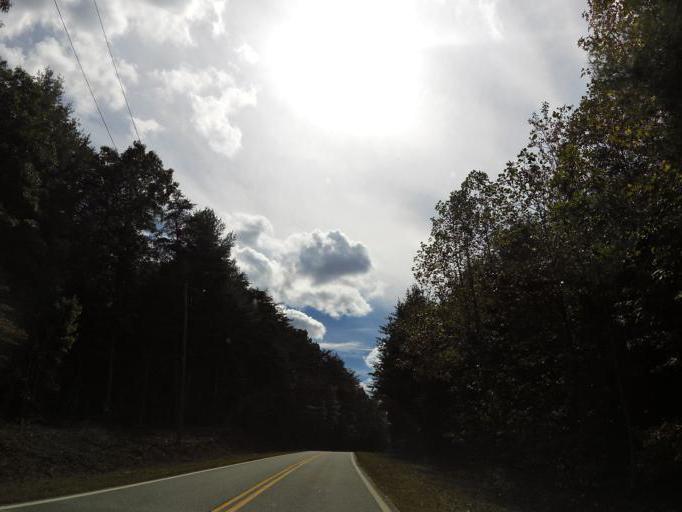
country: US
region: Georgia
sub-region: Pickens County
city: Jasper
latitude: 34.5240
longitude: -84.2781
